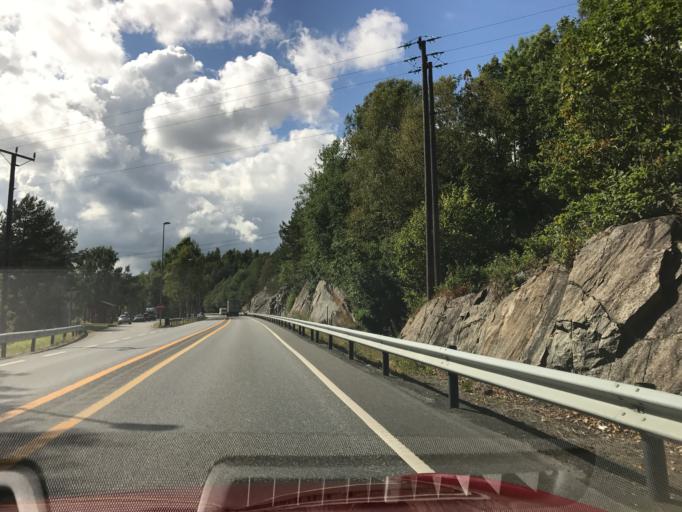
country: NO
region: Telemark
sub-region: Kragero
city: Kragero
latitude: 58.9609
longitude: 9.4513
